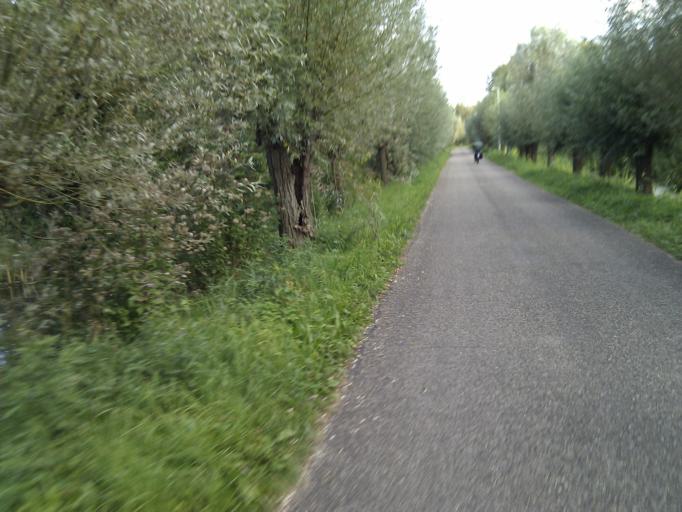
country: NL
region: Utrecht
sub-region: Gemeente De Bilt
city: De Bilt
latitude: 52.0957
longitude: 5.1548
